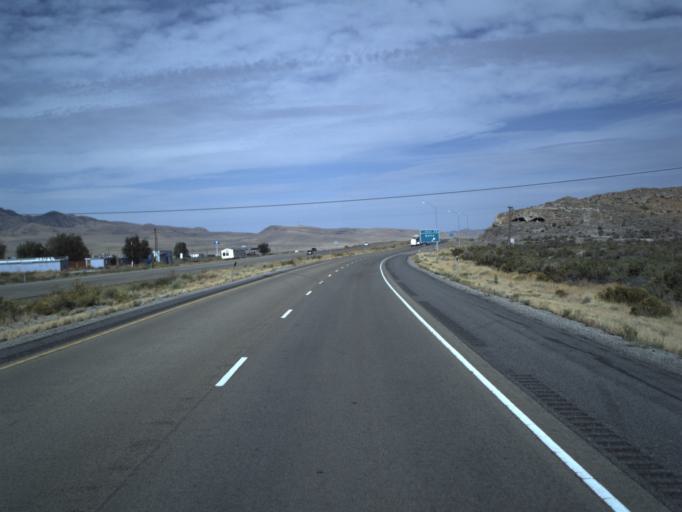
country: US
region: Utah
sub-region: Tooele County
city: Grantsville
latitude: 40.7594
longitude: -112.7744
